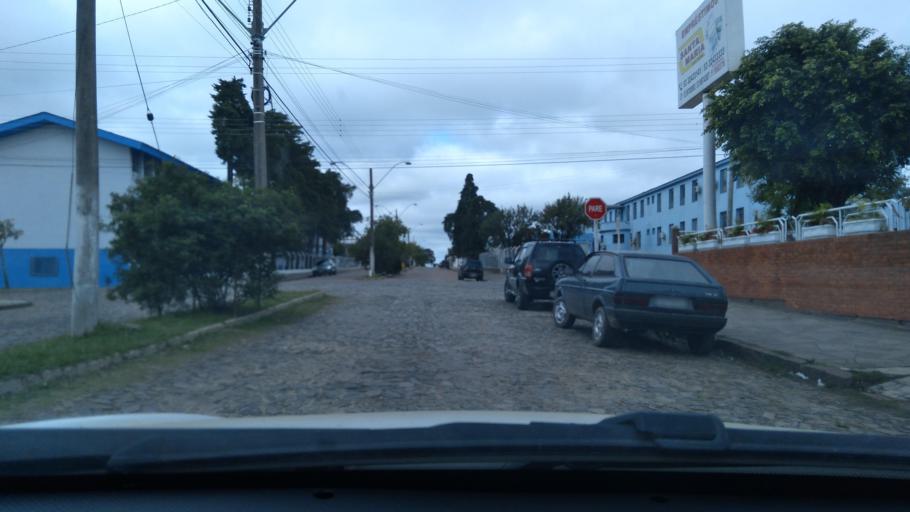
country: BR
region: Rio Grande do Sul
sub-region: Dom Pedrito
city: Dom Pedrito
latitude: -30.9807
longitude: -54.6707
